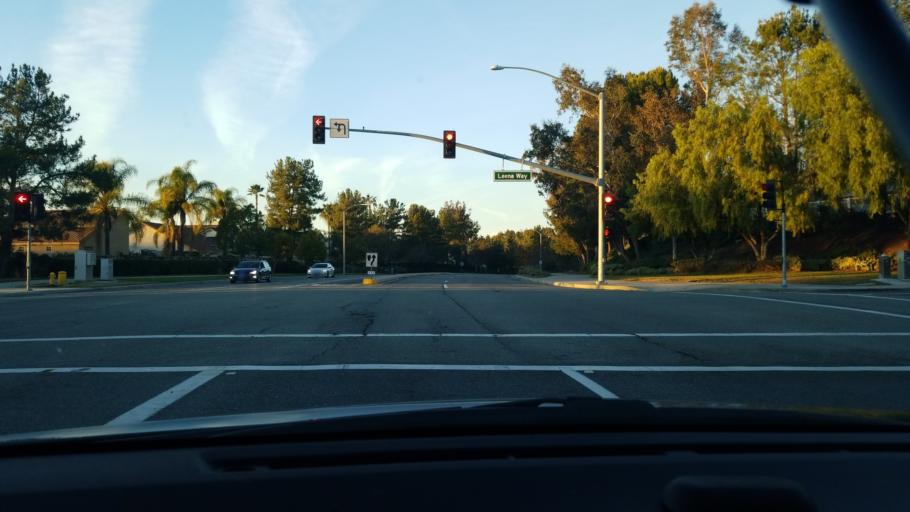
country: US
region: California
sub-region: Riverside County
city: Temecula
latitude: 33.4914
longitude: -117.0960
